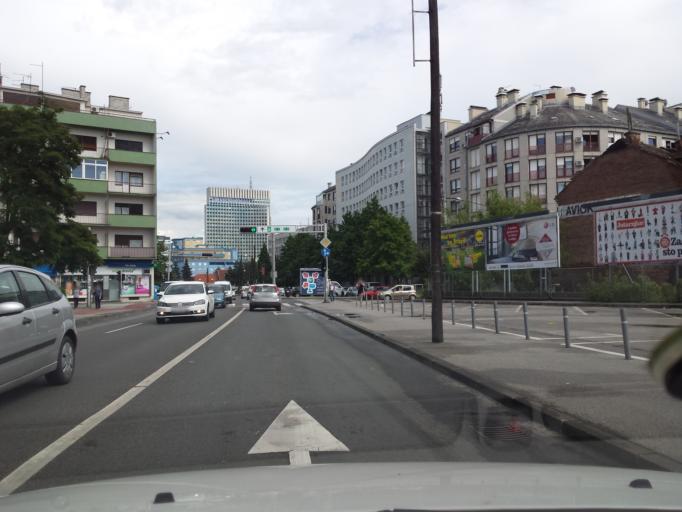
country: HR
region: Grad Zagreb
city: Zagreb - Centar
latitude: 45.7995
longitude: 15.9552
